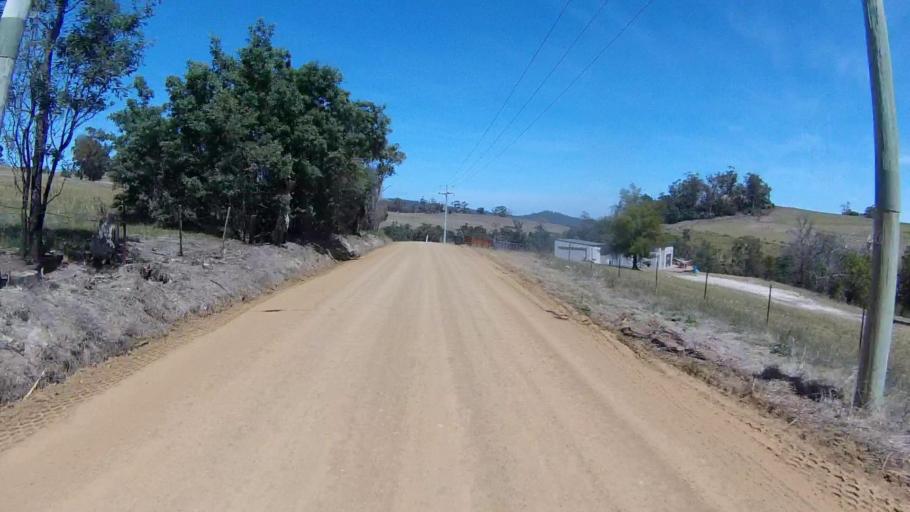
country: AU
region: Tasmania
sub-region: Sorell
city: Sorell
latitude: -42.7795
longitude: 147.6507
